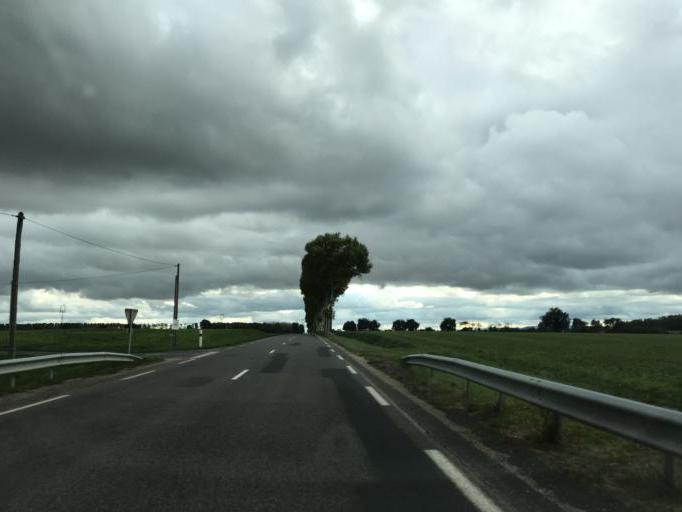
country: FR
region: Rhone-Alpes
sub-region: Departement de l'Ain
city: Saint-Trivier-sur-Moignans
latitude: 46.0472
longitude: 4.8689
